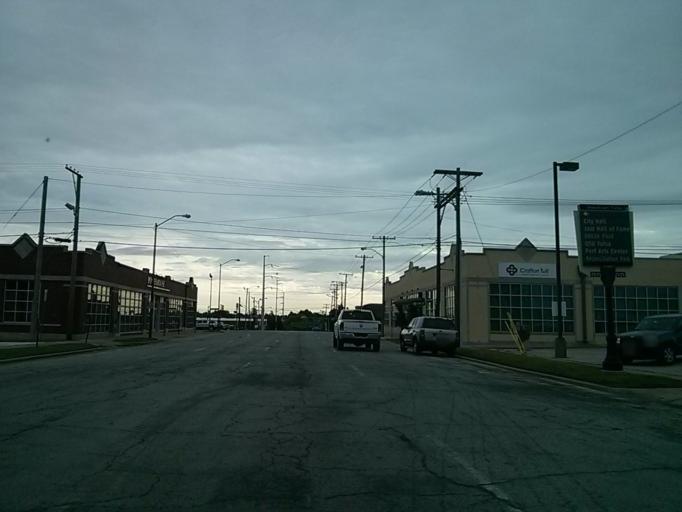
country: US
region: Oklahoma
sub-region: Tulsa County
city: Tulsa
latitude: 36.1494
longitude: -95.9861
